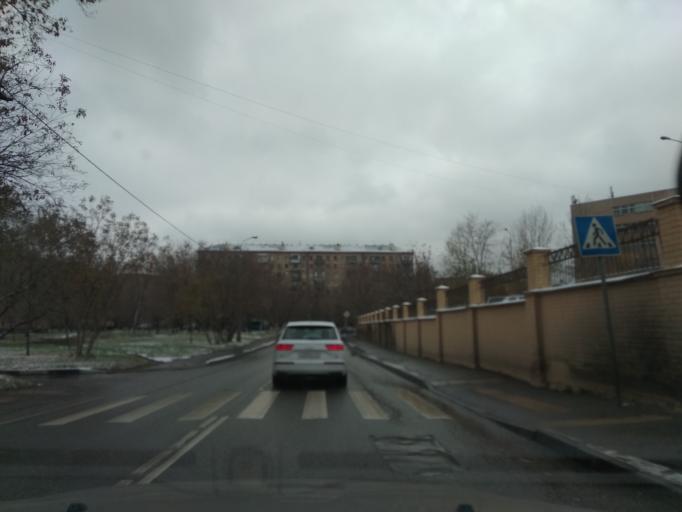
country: RU
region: Moscow
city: Pokrovskoye-Streshnevo
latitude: 55.7967
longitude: 37.4660
